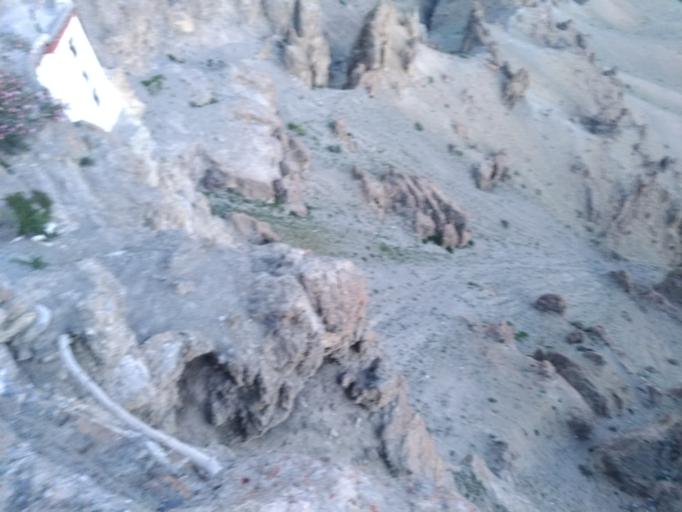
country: CN
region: Tibet Autonomous Region
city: Diyag
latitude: 32.0896
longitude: 78.2122
